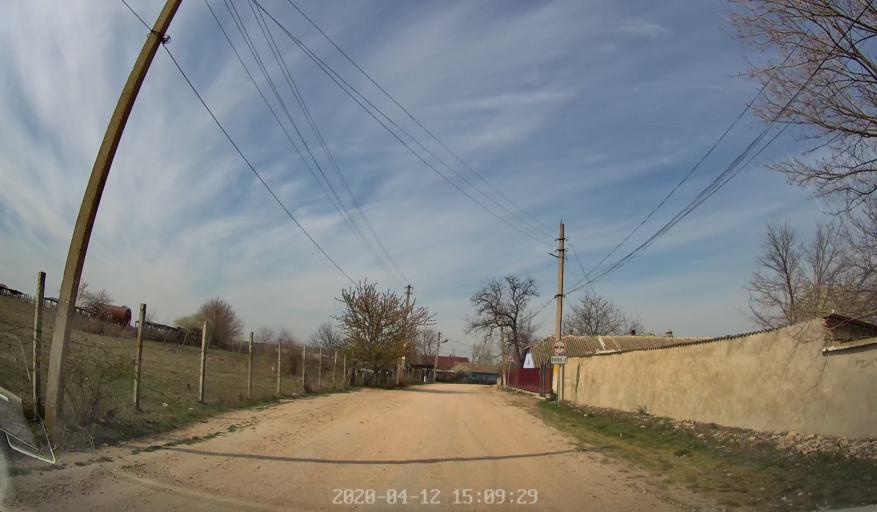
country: MD
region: Telenesti
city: Cocieri
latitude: 47.3203
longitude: 29.0686
